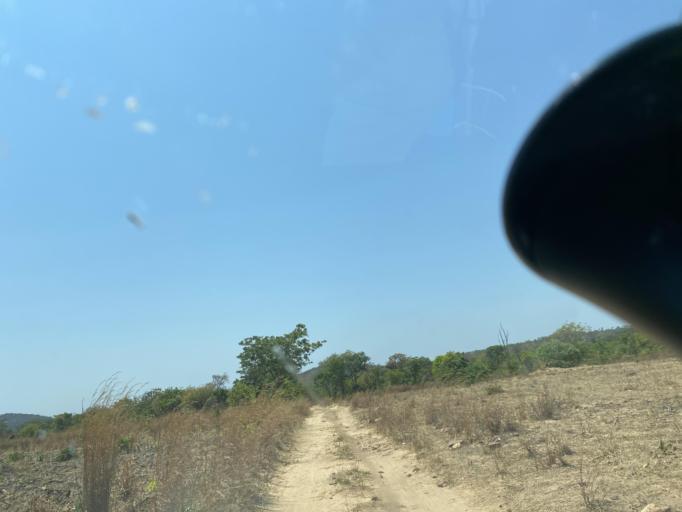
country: ZM
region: Lusaka
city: Chongwe
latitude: -15.4334
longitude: 29.1938
